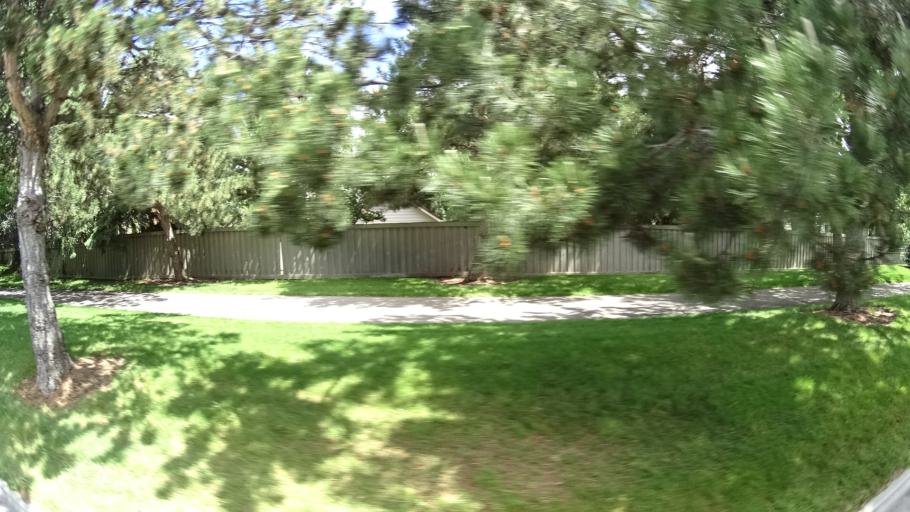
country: US
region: Idaho
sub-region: Ada County
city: Boise
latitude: 43.5799
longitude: -116.1612
